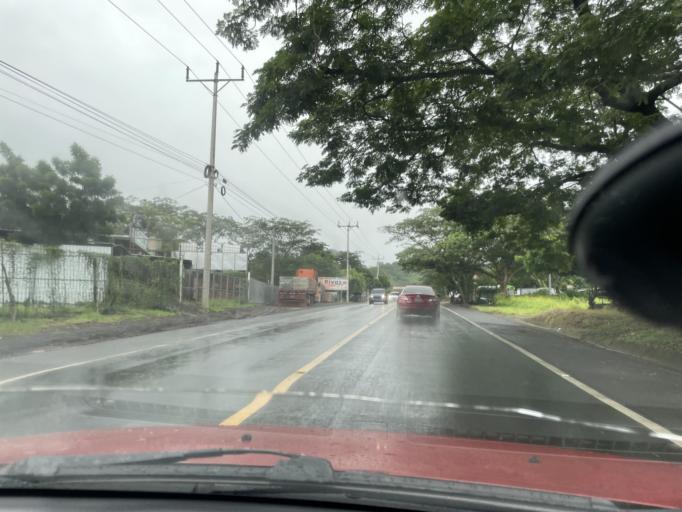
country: SV
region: San Miguel
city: San Miguel
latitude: 13.5453
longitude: -88.1190
